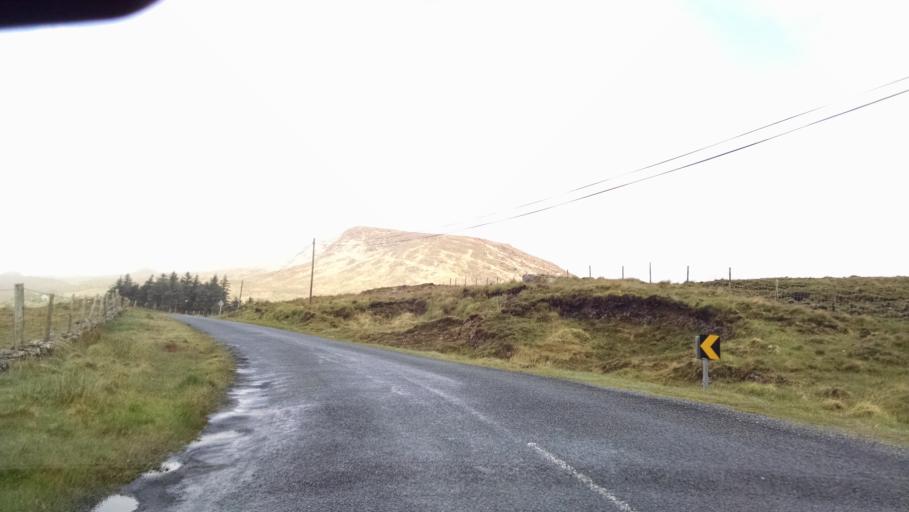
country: IE
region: Connaught
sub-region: Maigh Eo
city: Westport
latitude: 53.6063
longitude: -9.7436
